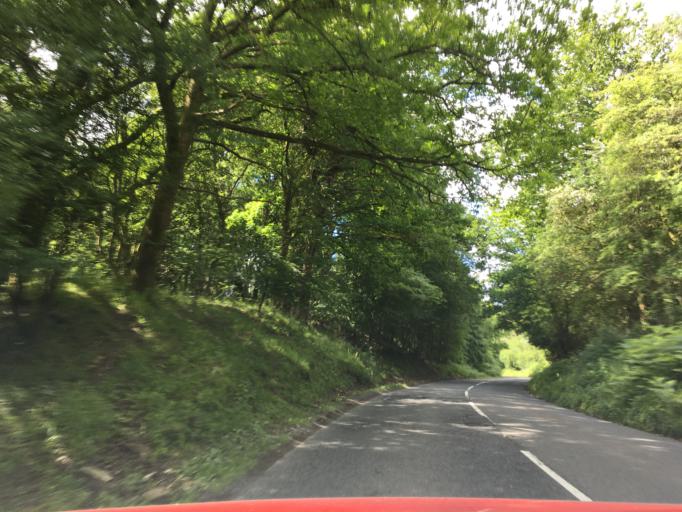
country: GB
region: England
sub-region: Gloucestershire
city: Bream
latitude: 51.7653
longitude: -2.5704
